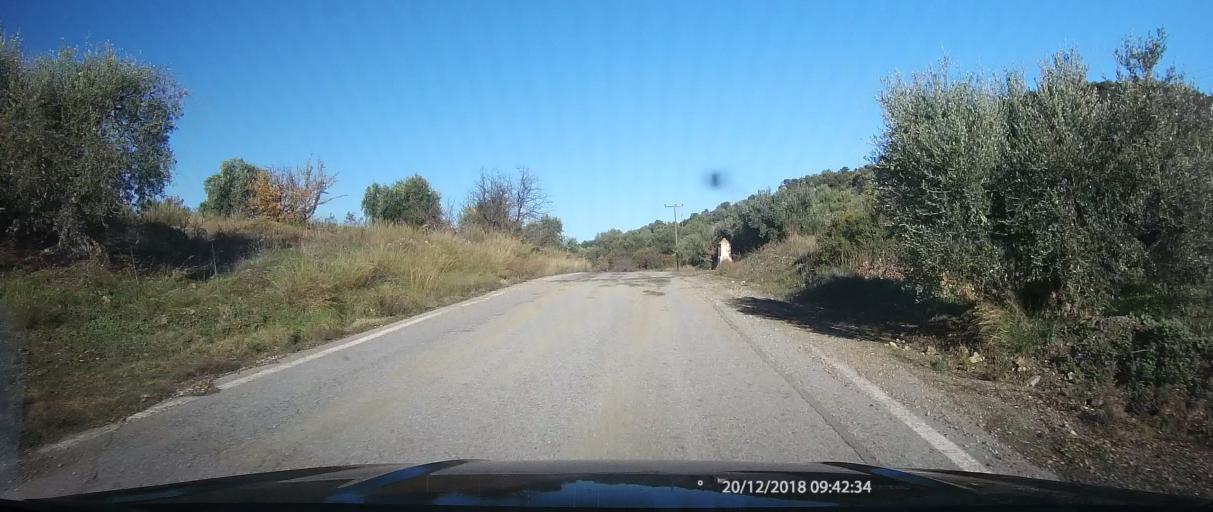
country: GR
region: Peloponnese
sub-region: Nomos Lakonias
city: Yerakion
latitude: 36.9615
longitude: 22.7527
